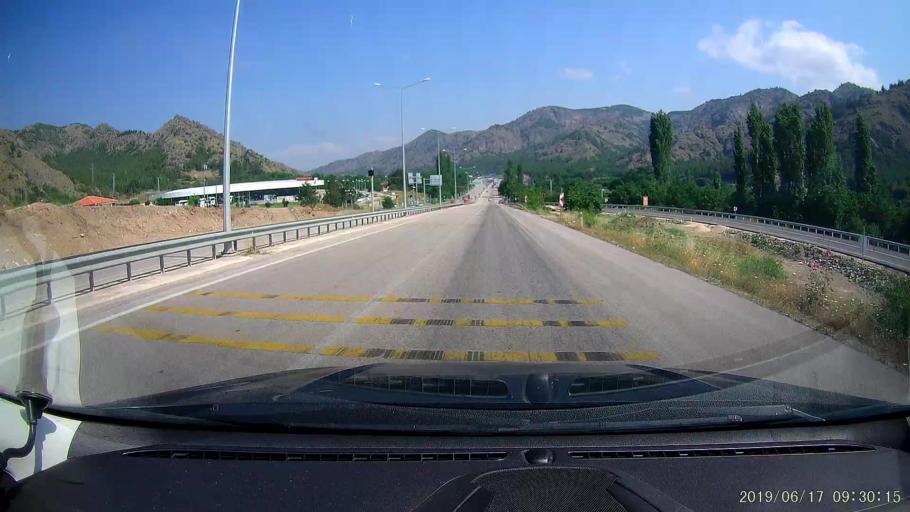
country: TR
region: Amasya
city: Amasya
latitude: 40.7040
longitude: 35.8050
